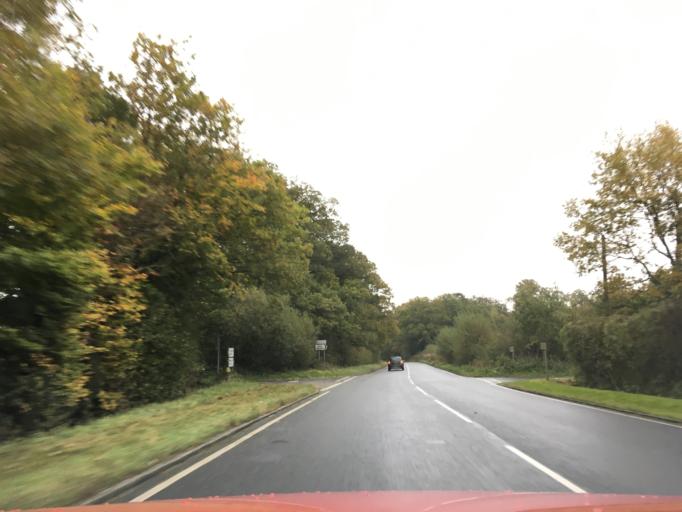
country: GB
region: England
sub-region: West Berkshire
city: Wickham
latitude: 51.4311
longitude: -1.4107
